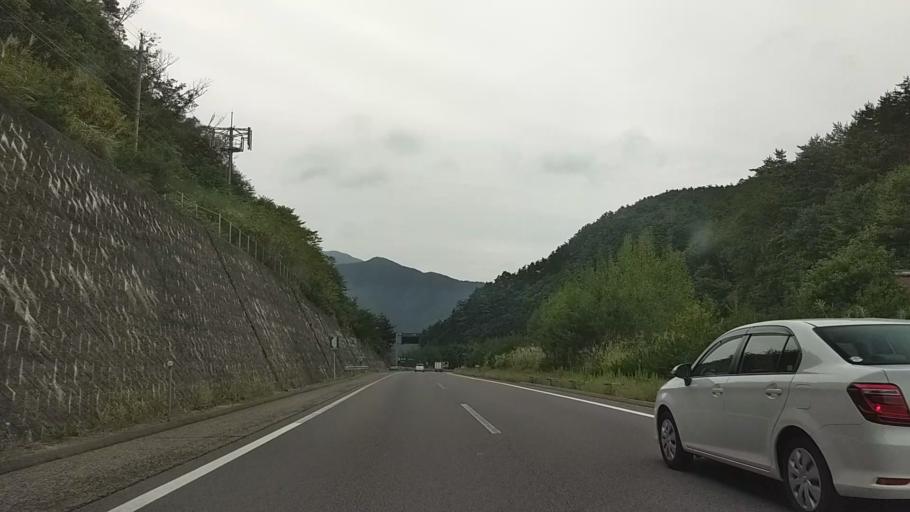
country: JP
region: Nagano
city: Omachi
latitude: 36.4639
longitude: 138.0669
